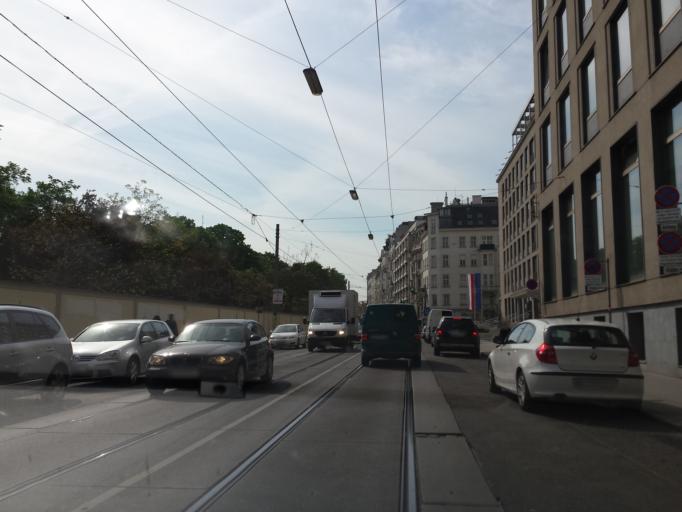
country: AT
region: Vienna
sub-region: Wien Stadt
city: Vienna
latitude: 48.1955
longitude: 16.3764
